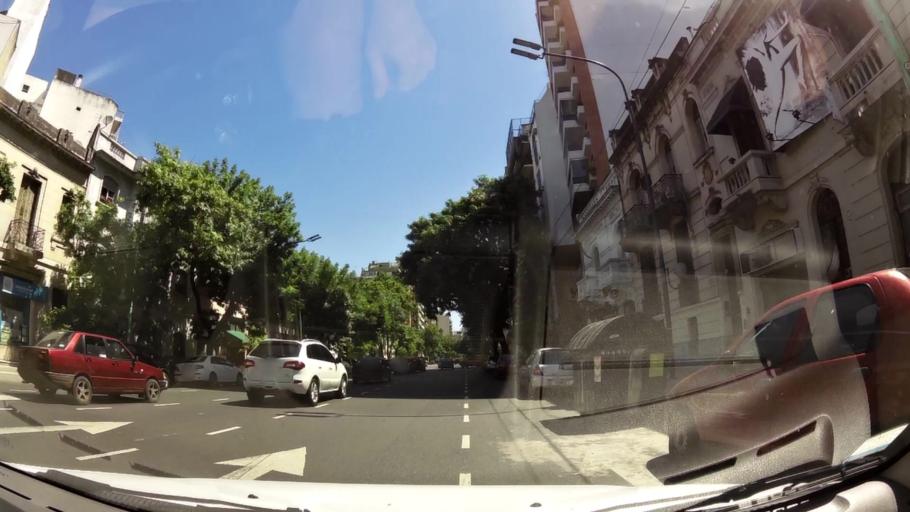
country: AR
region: Buenos Aires F.D.
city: Villa Santa Rita
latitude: -34.6231
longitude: -58.4438
